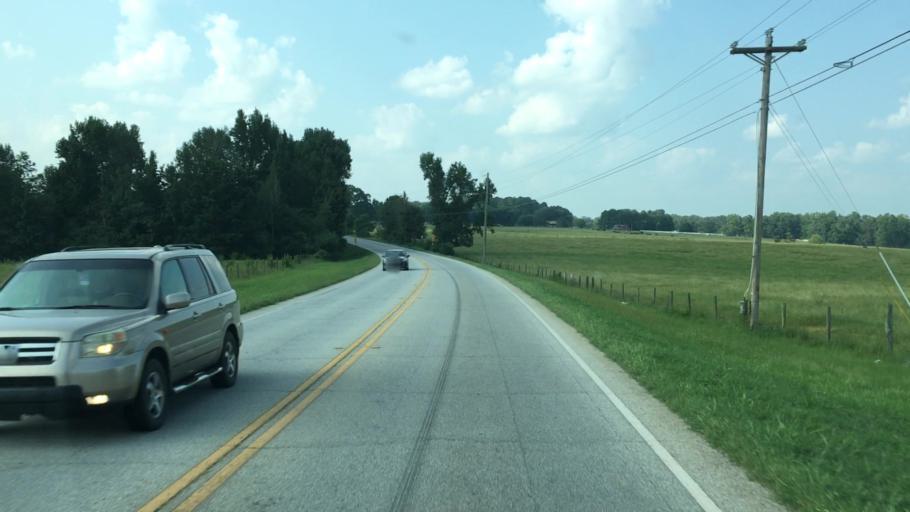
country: US
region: Georgia
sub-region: Walton County
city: Social Circle
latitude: 33.5614
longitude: -83.7360
